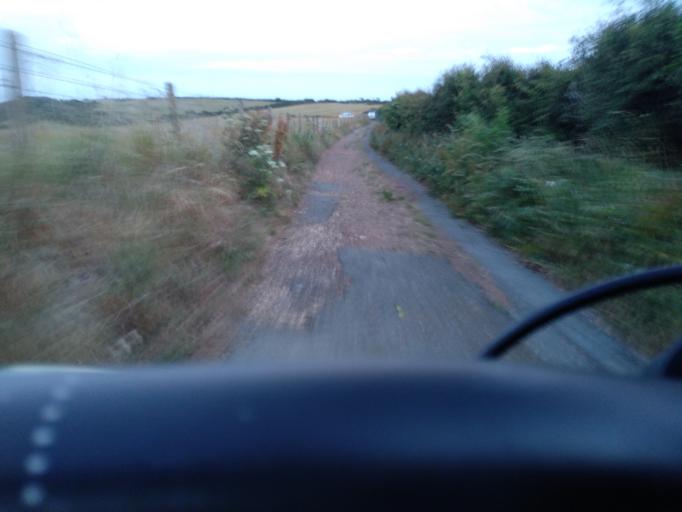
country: GB
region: England
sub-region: Isle of Wight
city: Ventnor
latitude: 50.6086
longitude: -1.2399
